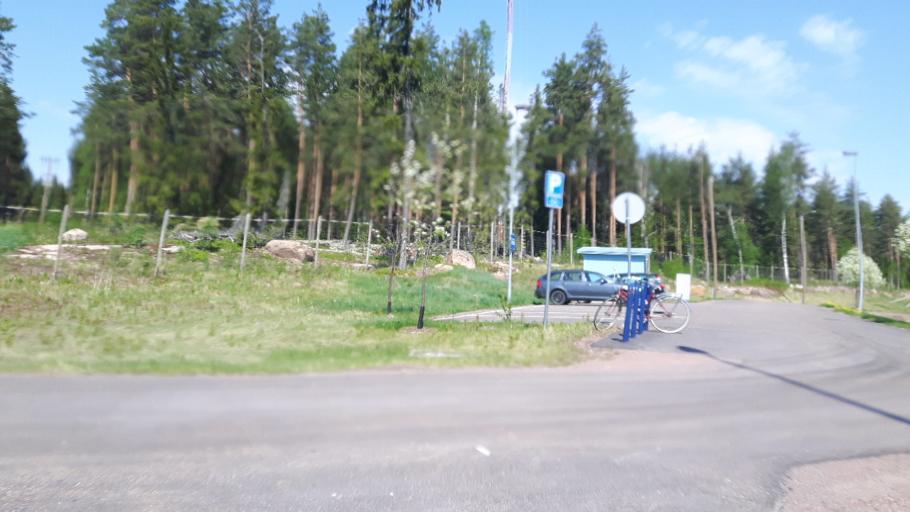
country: FI
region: Uusimaa
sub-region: Loviisa
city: Ruotsinpyhtaeae
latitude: 60.4932
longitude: 26.4193
